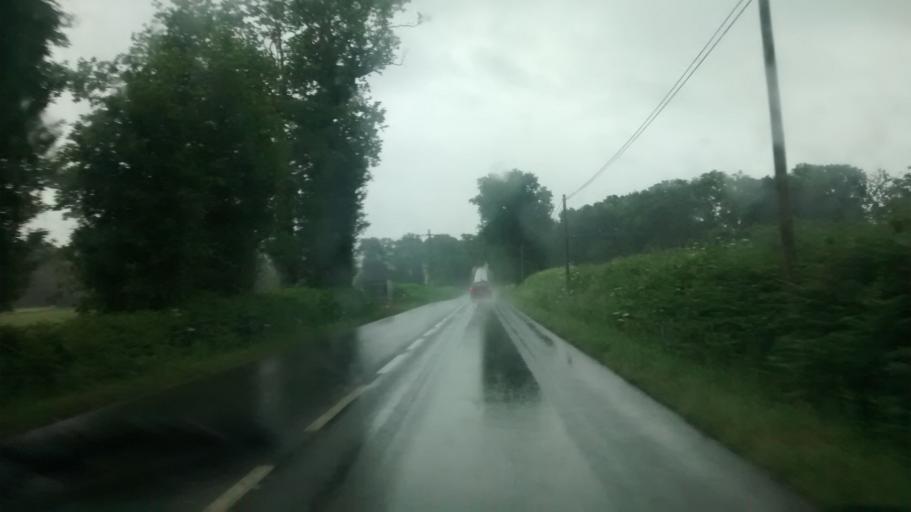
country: FR
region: Brittany
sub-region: Departement du Morbihan
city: La Gacilly
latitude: 47.7799
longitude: -2.1668
